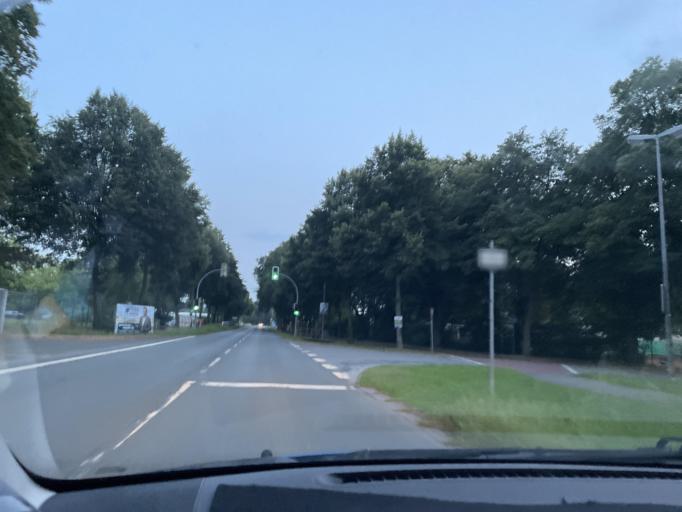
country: DE
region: Lower Saxony
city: Holzminden
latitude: 51.8364
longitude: 9.4681
